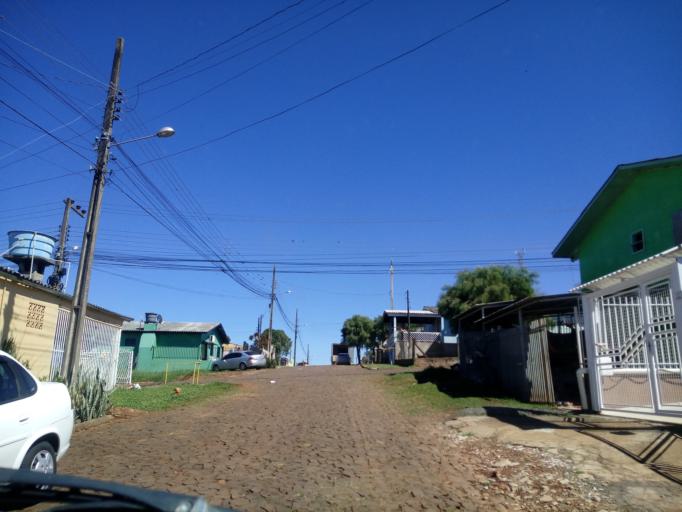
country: BR
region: Santa Catarina
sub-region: Chapeco
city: Chapeco
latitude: -27.0884
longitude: -52.6718
